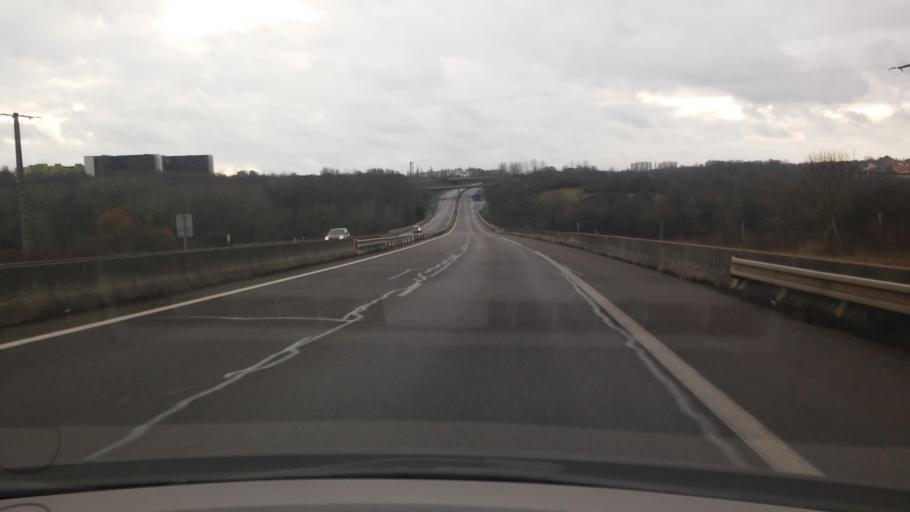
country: FR
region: Lorraine
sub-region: Departement de la Moselle
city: Saint-Julien-les-Metz
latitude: 49.1318
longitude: 6.2438
